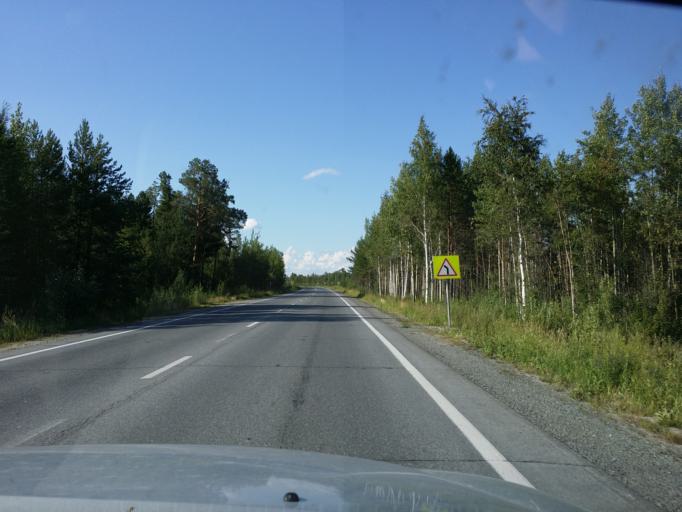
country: RU
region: Khanty-Mansiyskiy Avtonomnyy Okrug
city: Lokosovo
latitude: 61.3843
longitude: 74.9208
